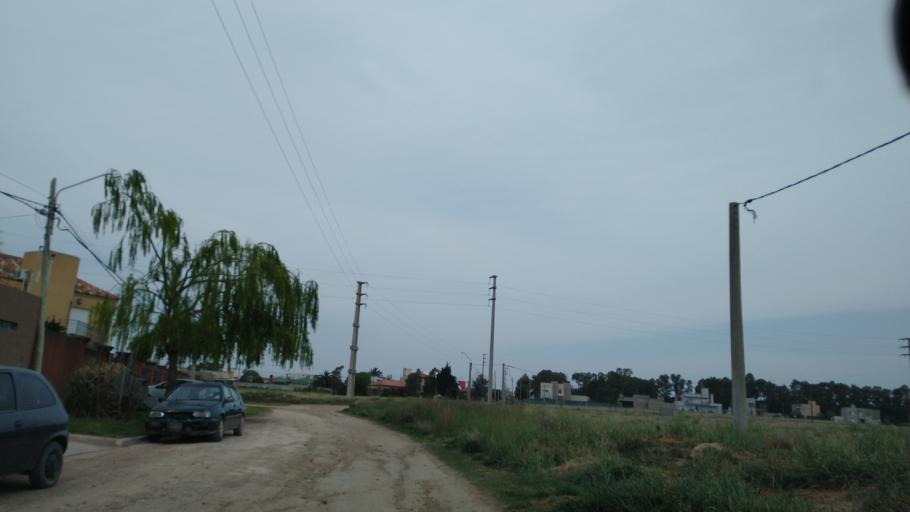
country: AR
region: Buenos Aires
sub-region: Partido de Bahia Blanca
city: Bahia Blanca
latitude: -38.7007
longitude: -62.2270
